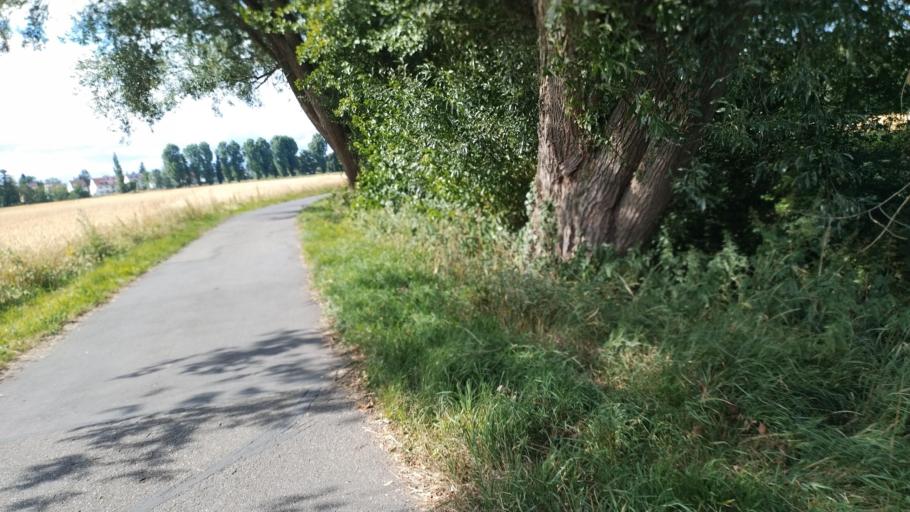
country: DE
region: Baden-Wuerttemberg
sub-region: Karlsruhe Region
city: Karlsruhe
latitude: 48.9766
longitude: 8.3990
